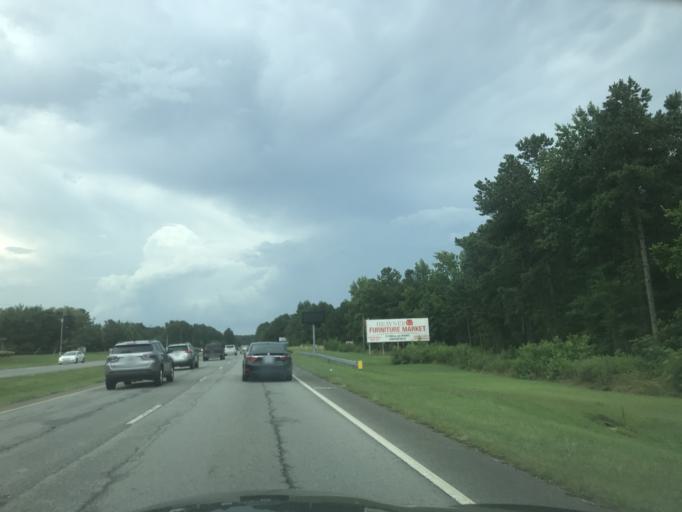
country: US
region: North Carolina
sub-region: Johnston County
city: Clayton
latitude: 35.6627
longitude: -78.4917
